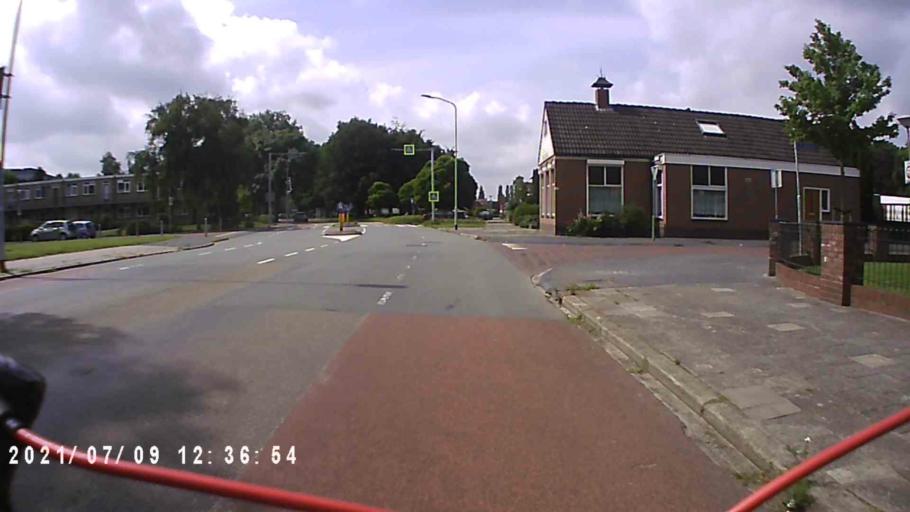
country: NL
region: Groningen
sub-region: Gemeente  Oldambt
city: Winschoten
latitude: 53.1468
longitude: 7.0238
